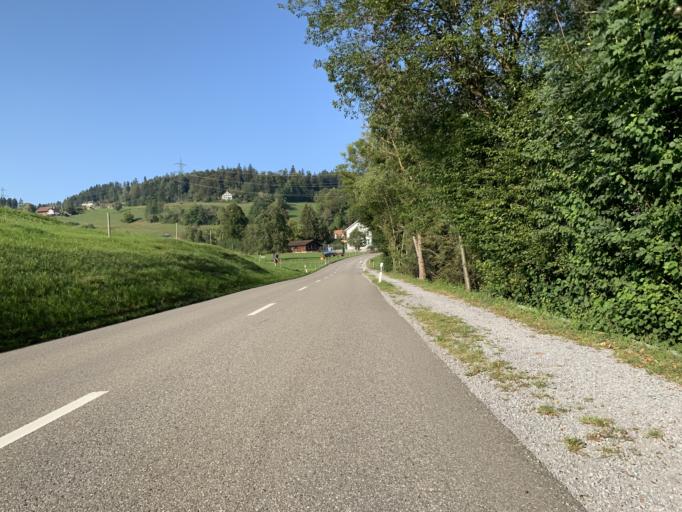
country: CH
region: Zurich
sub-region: Bezirk Hinwil
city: Hinwil
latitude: 47.3128
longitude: 8.8539
